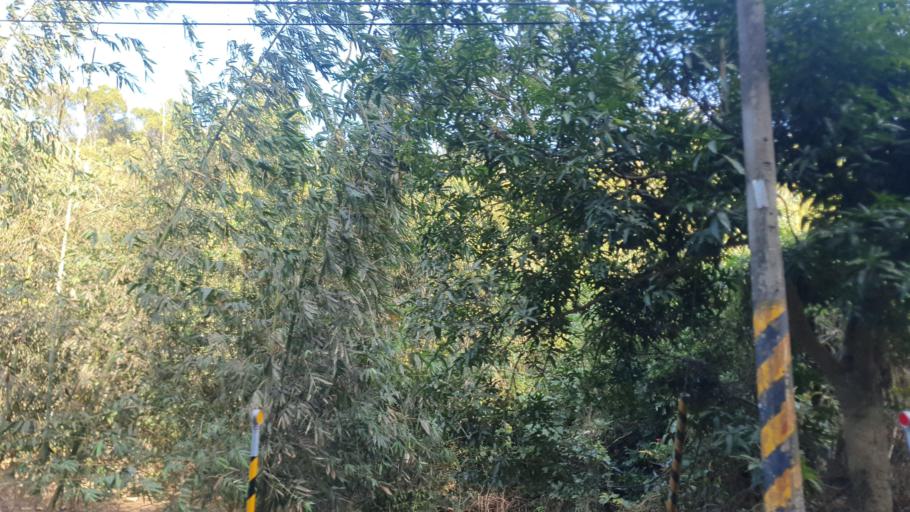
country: TW
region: Taiwan
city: Yujing
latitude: 23.0083
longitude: 120.3881
